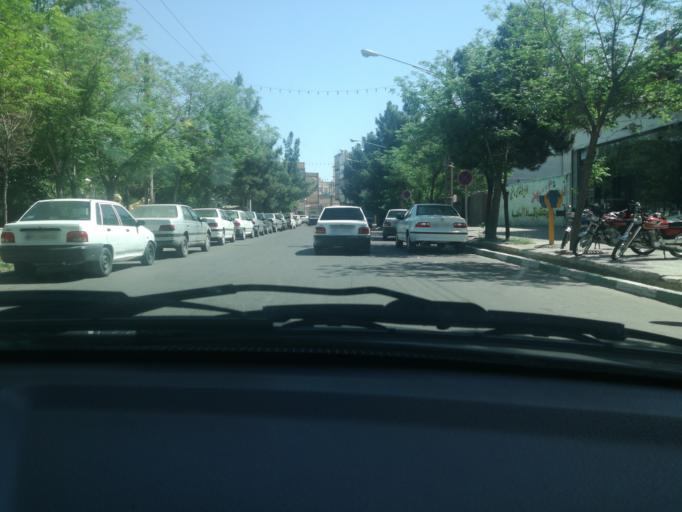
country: IR
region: Razavi Khorasan
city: Sarakhs
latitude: 36.5346
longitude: 61.1623
